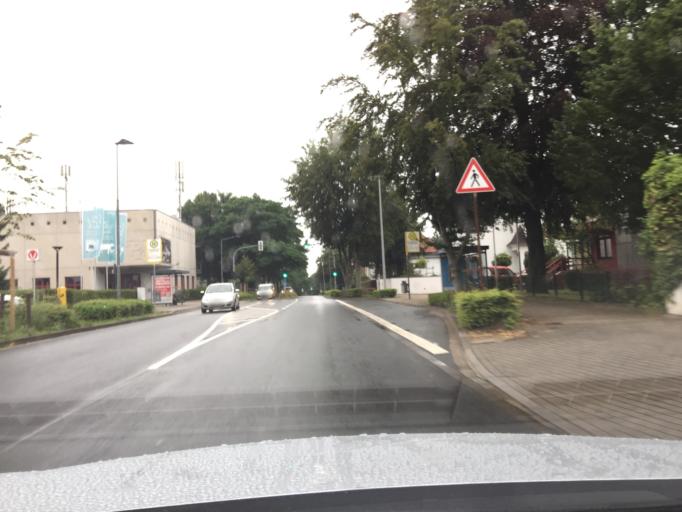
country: DE
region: North Rhine-Westphalia
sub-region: Regierungsbezirk Dusseldorf
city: Ratingen
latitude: 51.3358
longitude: 6.9013
